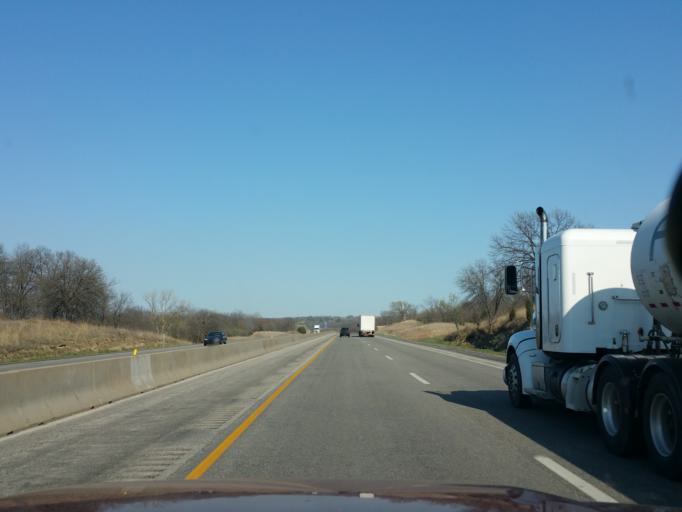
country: US
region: Kansas
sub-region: Leavenworth County
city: Basehor
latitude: 39.0838
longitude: -94.9380
